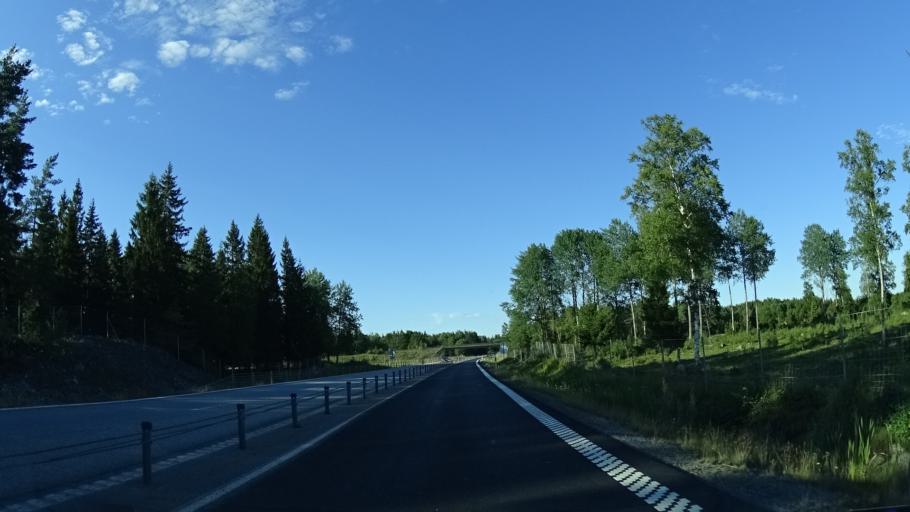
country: SE
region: Stockholm
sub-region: Osterakers Kommun
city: Akersberga
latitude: 59.6072
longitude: 18.2792
